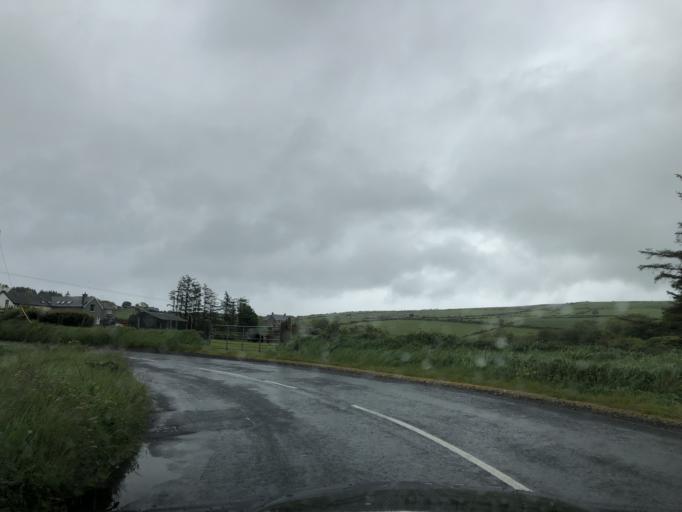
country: GB
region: Northern Ireland
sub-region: Moyle District
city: Ballycastle
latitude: 55.1999
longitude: -6.1736
